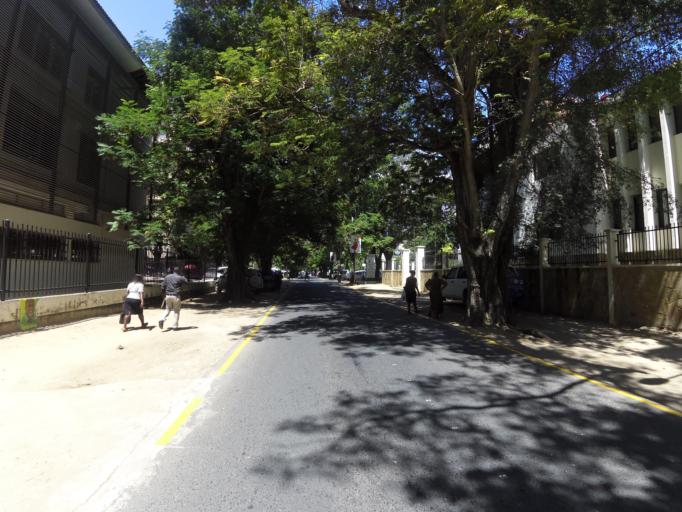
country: TZ
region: Dar es Salaam
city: Dar es Salaam
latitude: -6.8130
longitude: 39.2938
